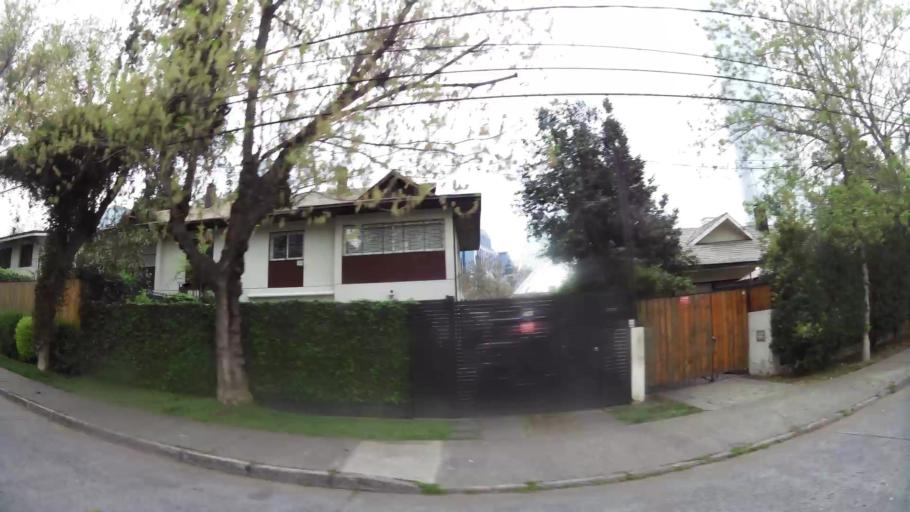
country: CL
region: Santiago Metropolitan
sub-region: Provincia de Santiago
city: Villa Presidente Frei, Nunoa, Santiago, Chile
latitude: -33.4145
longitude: -70.6090
